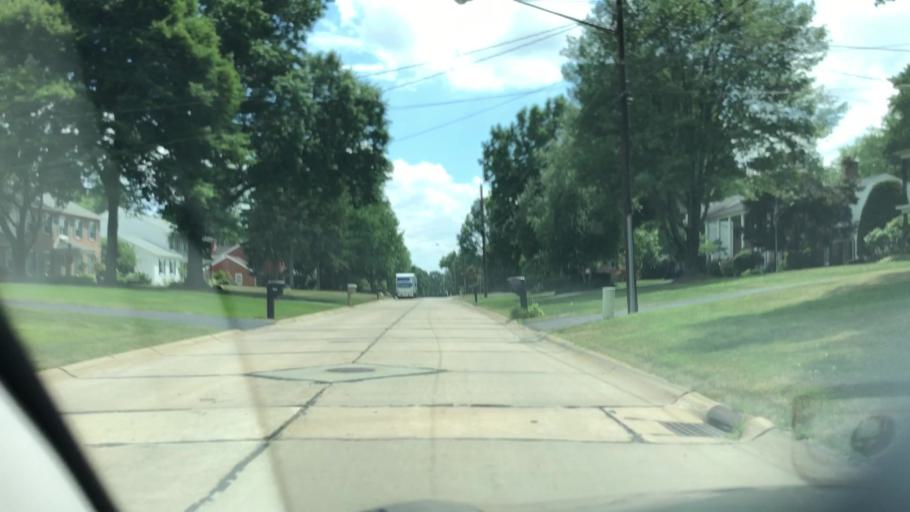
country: US
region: Ohio
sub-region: Summit County
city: Fairlawn
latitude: 41.1318
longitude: -81.6235
